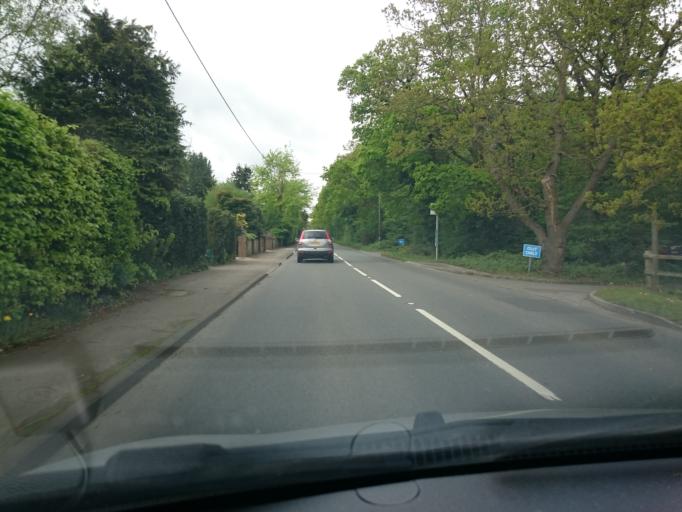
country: GB
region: England
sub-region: Surrey
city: Normandy
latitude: 51.2567
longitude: -0.6678
